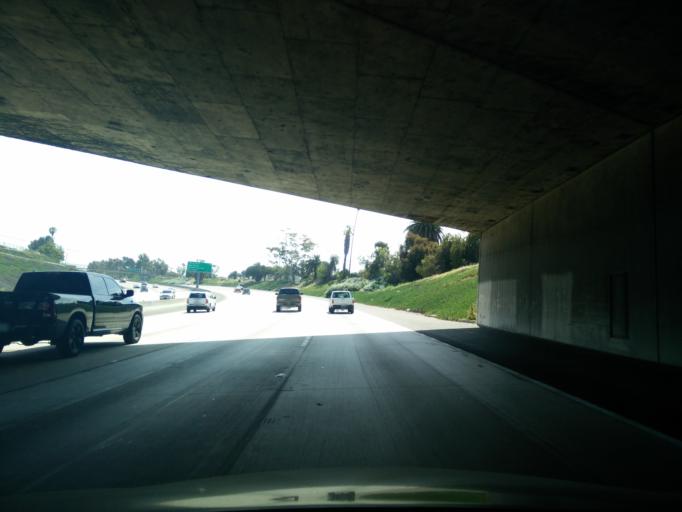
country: US
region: California
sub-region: San Diego County
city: San Diego
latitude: 32.6949
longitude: -117.1339
